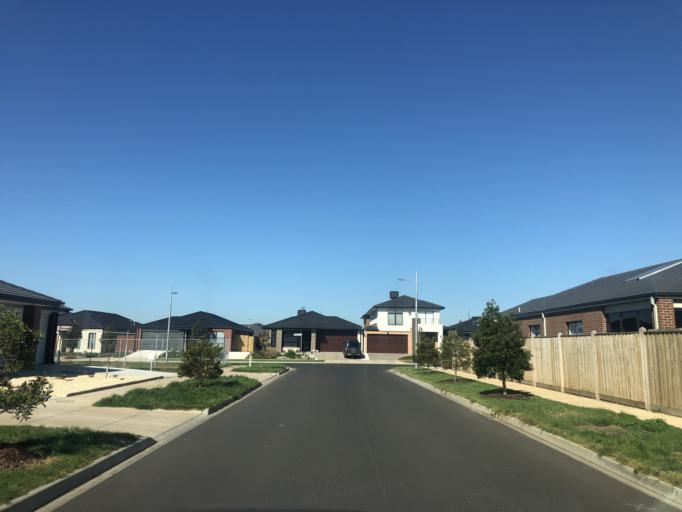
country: AU
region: Victoria
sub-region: Wyndham
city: Hoppers Crossing
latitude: -37.9093
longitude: 144.7167
